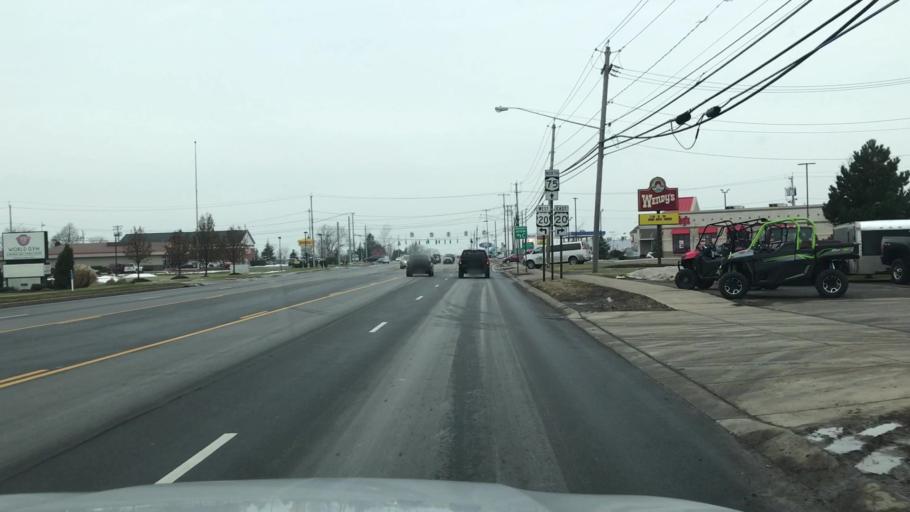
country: US
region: New York
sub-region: Erie County
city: Hamburg
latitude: 42.7479
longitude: -78.8531
